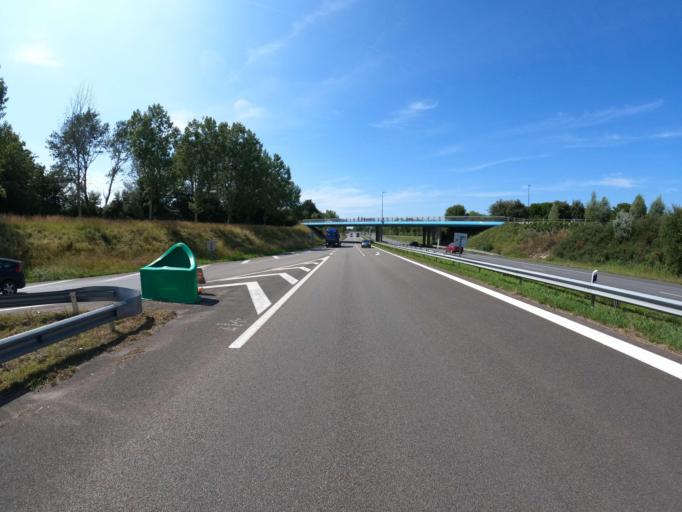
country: FR
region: Pays de la Loire
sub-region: Departement de la Loire-Atlantique
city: Pornic
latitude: 47.1122
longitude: -2.0768
